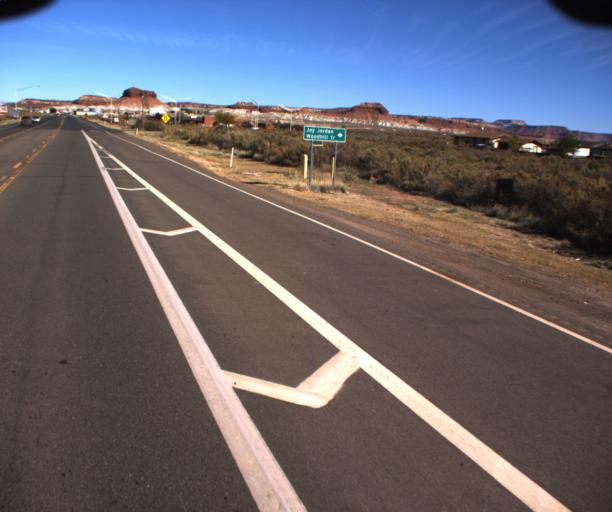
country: US
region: Arizona
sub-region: Coconino County
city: Fredonia
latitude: 36.9603
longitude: -112.5269
